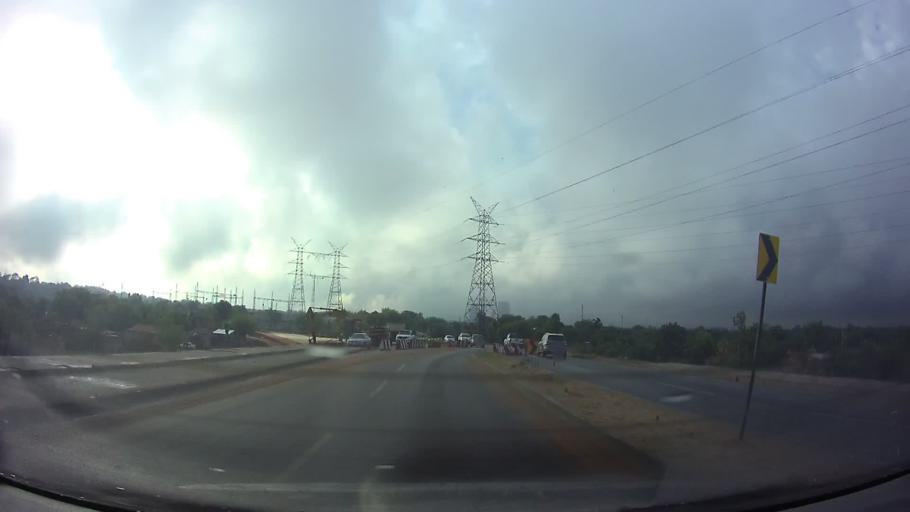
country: PY
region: Asuncion
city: Asuncion
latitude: -25.2465
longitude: -57.5883
